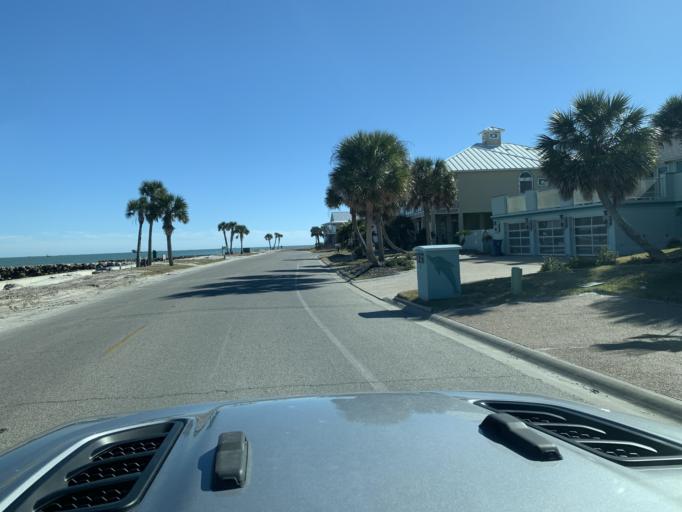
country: US
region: Texas
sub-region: Aransas County
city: Fulton
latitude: 28.0376
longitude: -97.0257
